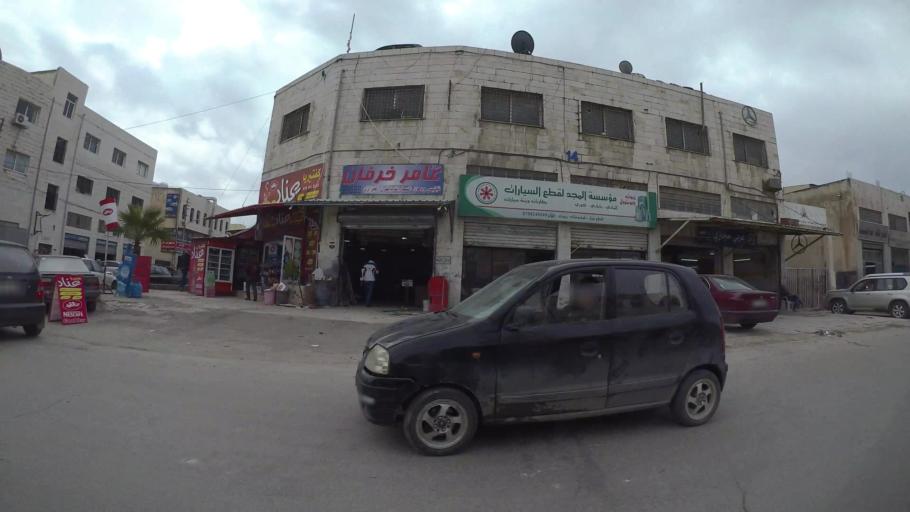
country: JO
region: Amman
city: Wadi as Sir
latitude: 31.9445
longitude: 35.8408
